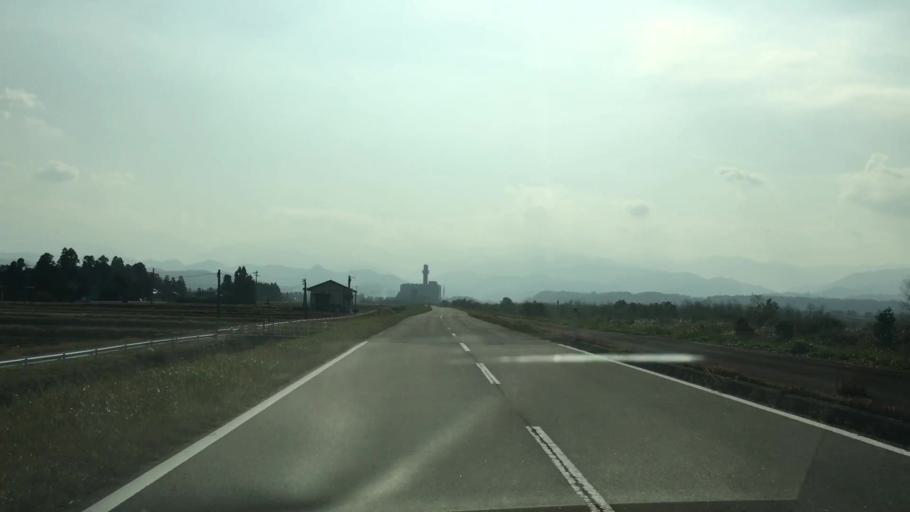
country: JP
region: Toyama
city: Toyama-shi
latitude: 36.6381
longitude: 137.2903
